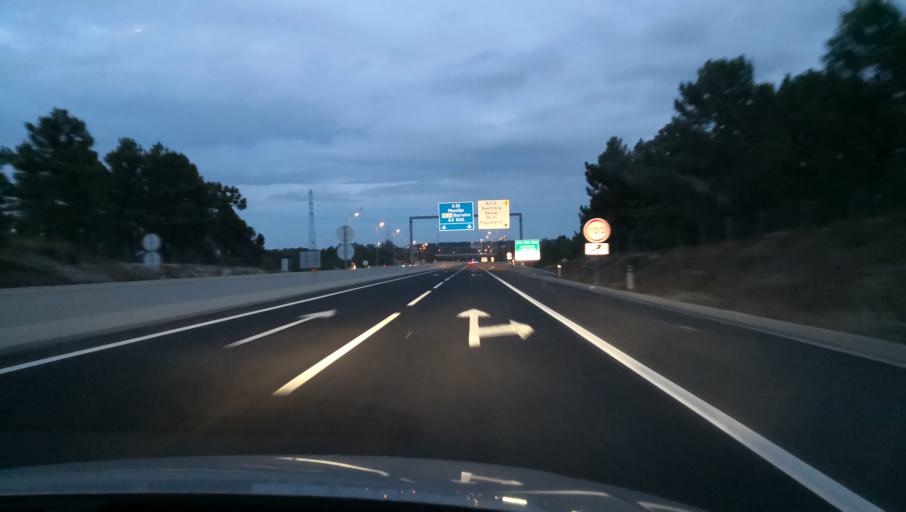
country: PT
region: Setubal
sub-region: Seixal
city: Arrentela
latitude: 38.6026
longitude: -9.1172
